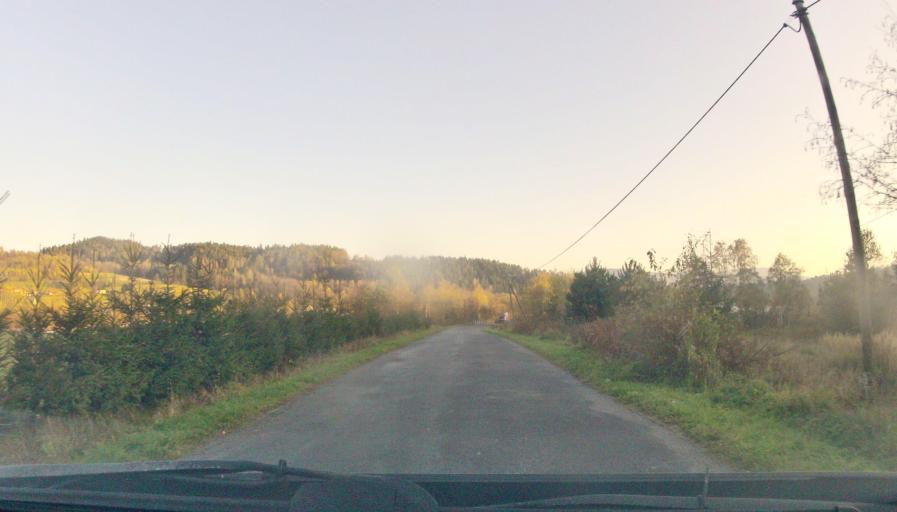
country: PL
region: Lesser Poland Voivodeship
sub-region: Powiat suski
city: Krzeszow
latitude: 49.7508
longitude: 19.4631
